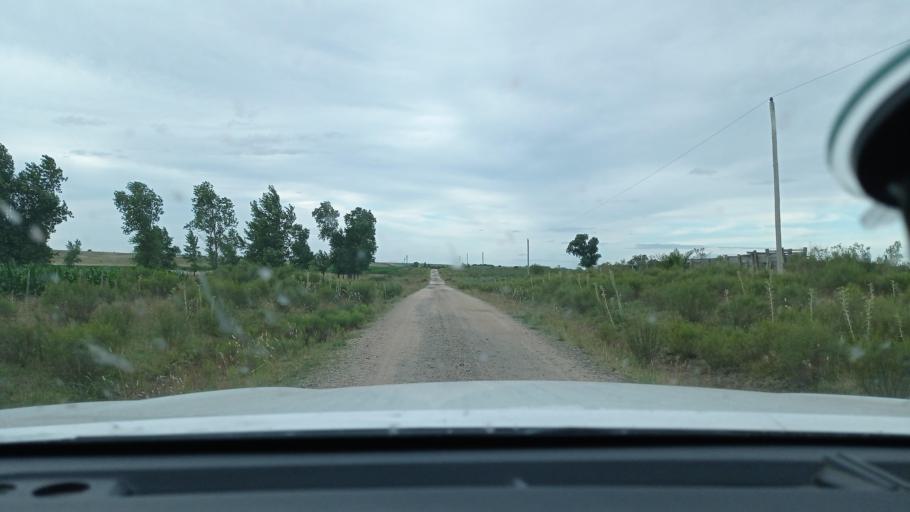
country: UY
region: Florida
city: Casupa
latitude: -34.1285
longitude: -55.7766
